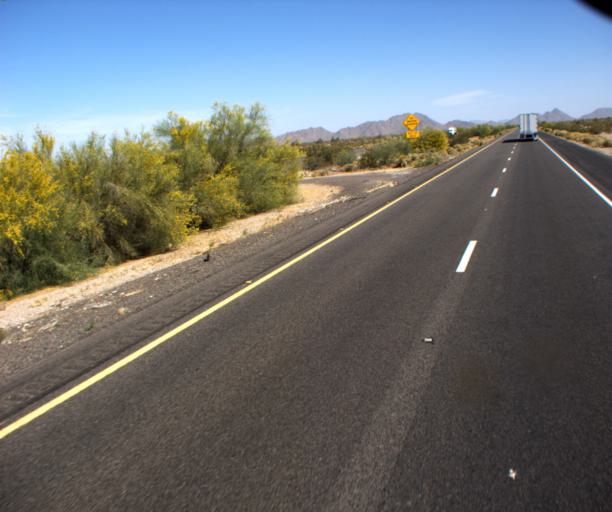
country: US
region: Arizona
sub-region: Maricopa County
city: Gila Bend
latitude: 32.9229
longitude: -112.6609
